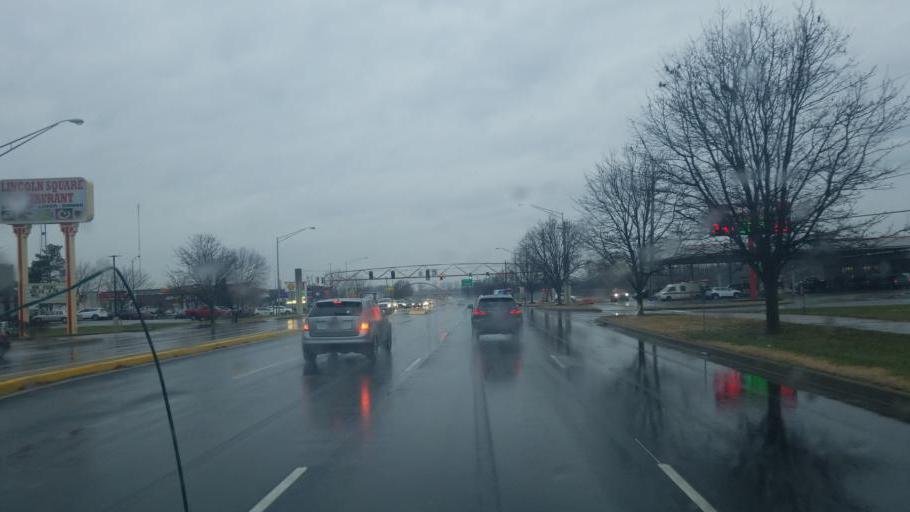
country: US
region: Indiana
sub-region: Bartholomew County
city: Columbus
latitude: 39.2005
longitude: -85.9498
